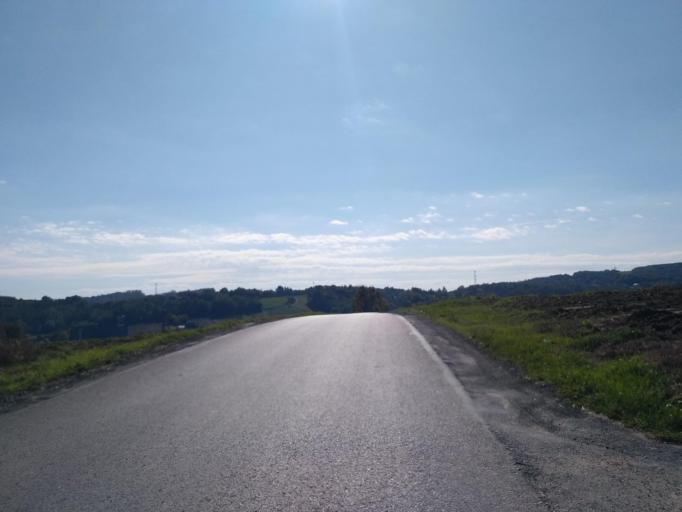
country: PL
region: Subcarpathian Voivodeship
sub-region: Powiat debicki
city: Slotowa
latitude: 49.9498
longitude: 21.2908
